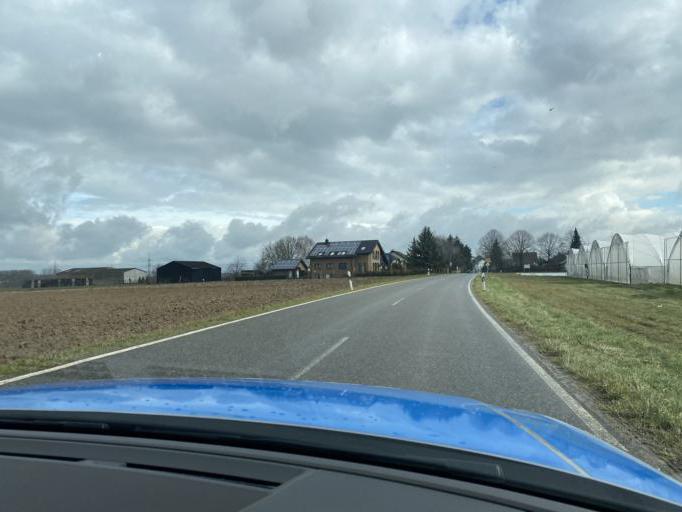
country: DE
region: North Rhine-Westphalia
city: Meckenheim
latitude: 50.5923
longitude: 7.0535
